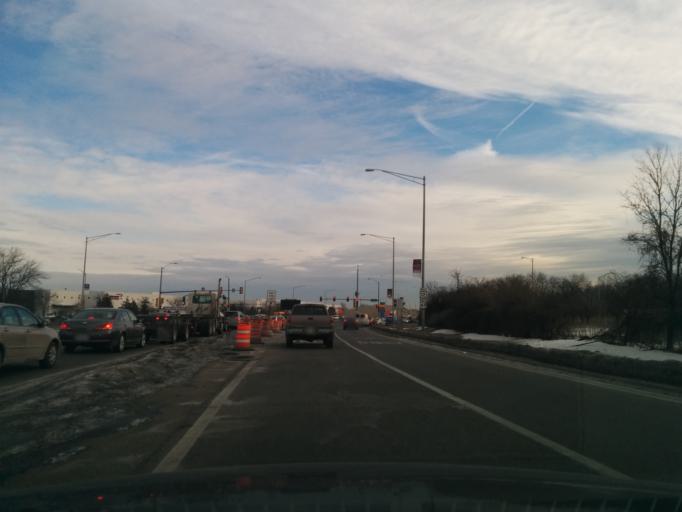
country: US
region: Illinois
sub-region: Cook County
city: Schiller Park
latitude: 41.9562
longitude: -87.8850
